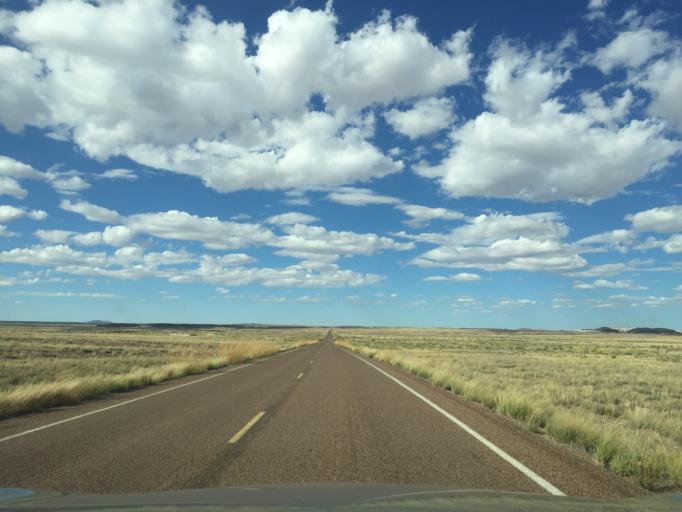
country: US
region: Arizona
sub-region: Navajo County
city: Holbrook
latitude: 34.9076
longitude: -109.7858
